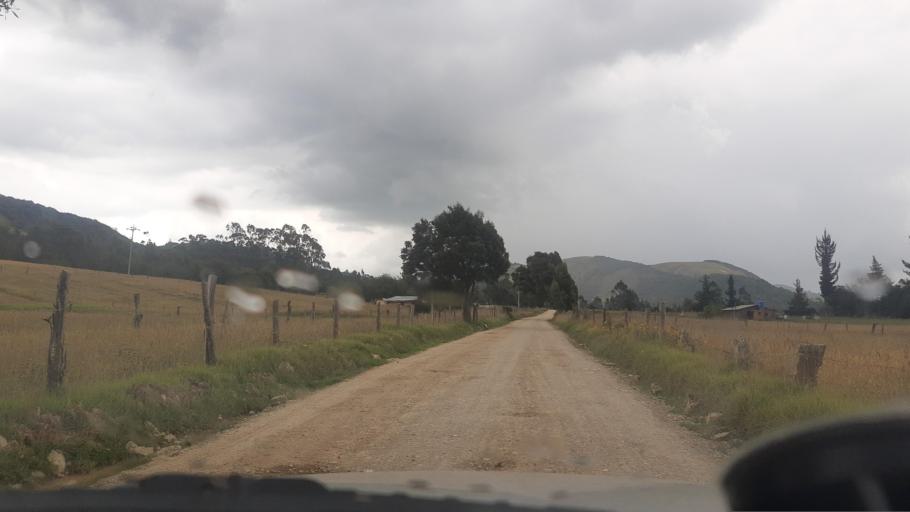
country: CO
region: Cundinamarca
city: Cucunuba
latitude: 5.1849
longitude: -73.7985
